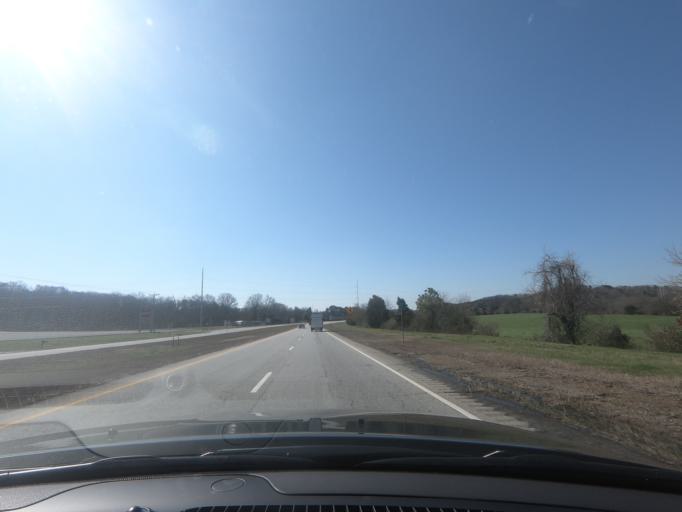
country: US
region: Georgia
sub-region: Gordon County
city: Calhoun
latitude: 34.4680
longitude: -84.9768
